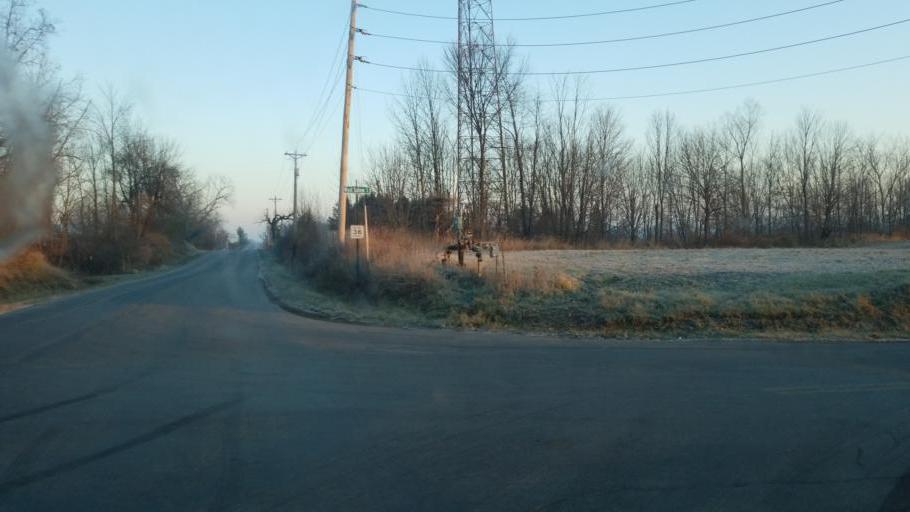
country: US
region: Ohio
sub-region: Wayne County
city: West Salem
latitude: 40.9866
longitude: -82.0546
